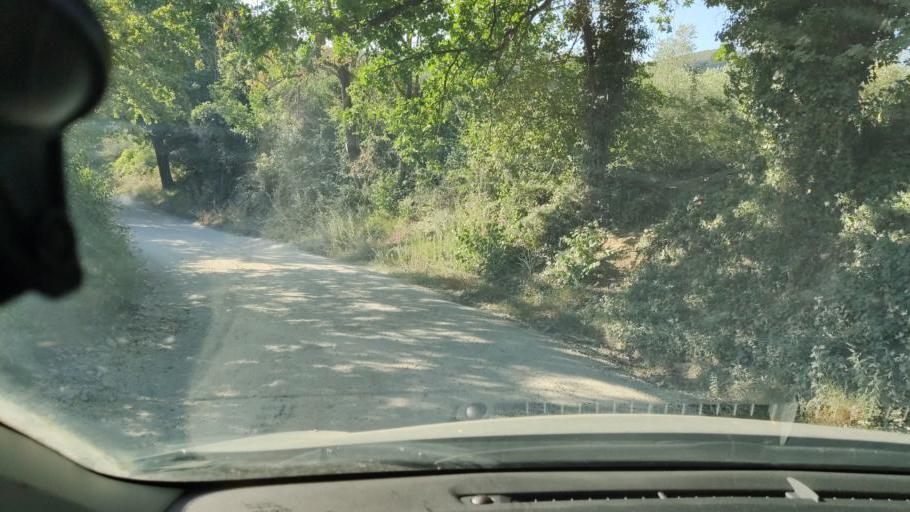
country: IT
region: Umbria
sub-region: Provincia di Terni
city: Amelia
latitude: 42.5451
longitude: 12.3930
